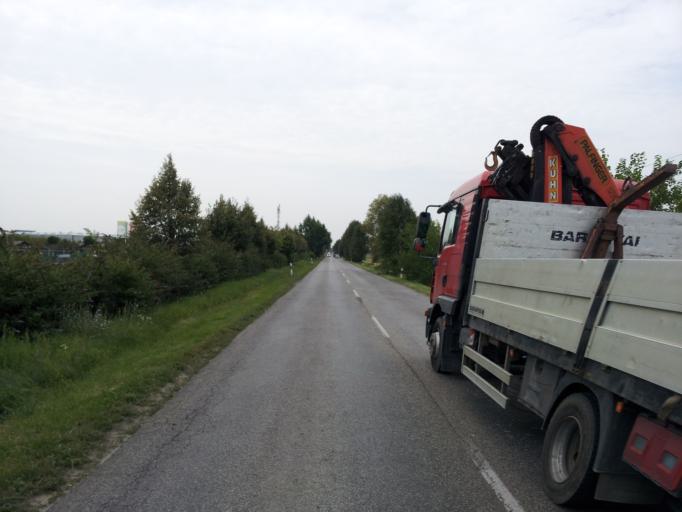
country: HU
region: Pest
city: Szigetszentmiklos
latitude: 47.3648
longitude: 19.0480
